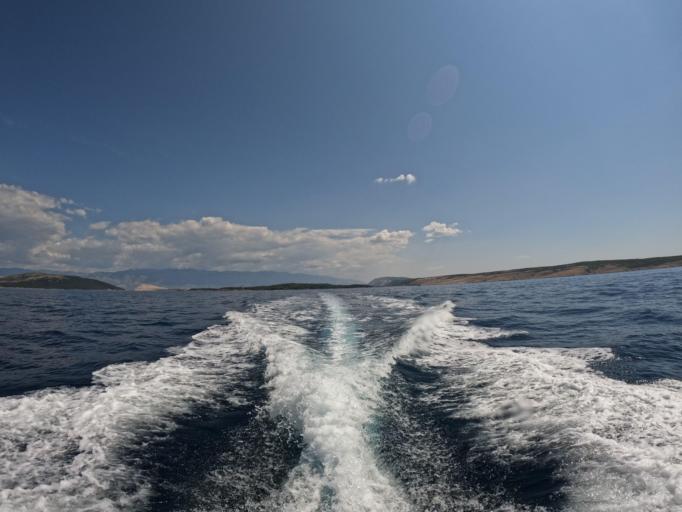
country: HR
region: Primorsko-Goranska
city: Lopar
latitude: 44.8593
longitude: 14.6967
